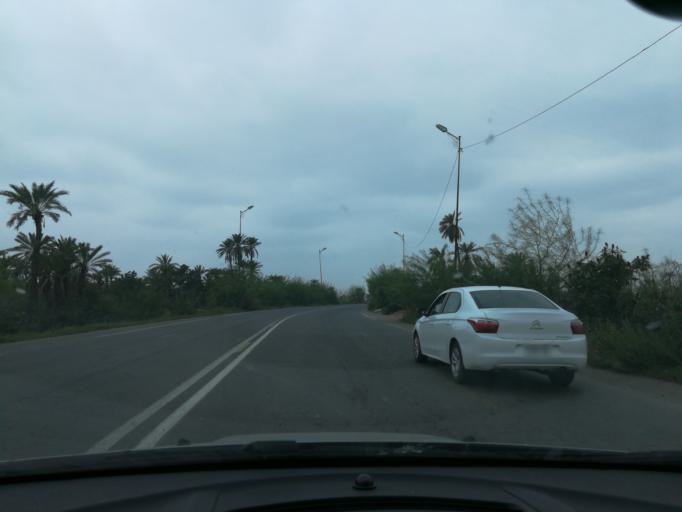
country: MA
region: Marrakech-Tensift-Al Haouz
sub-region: Marrakech
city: Marrakesh
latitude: 31.6879
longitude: -8.0221
